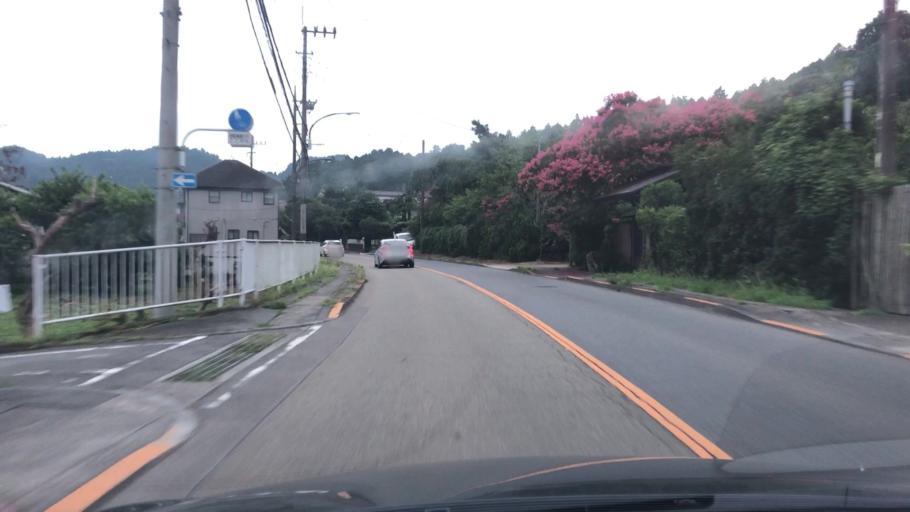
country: JP
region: Tokyo
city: Itsukaichi
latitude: 35.7501
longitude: 139.2403
